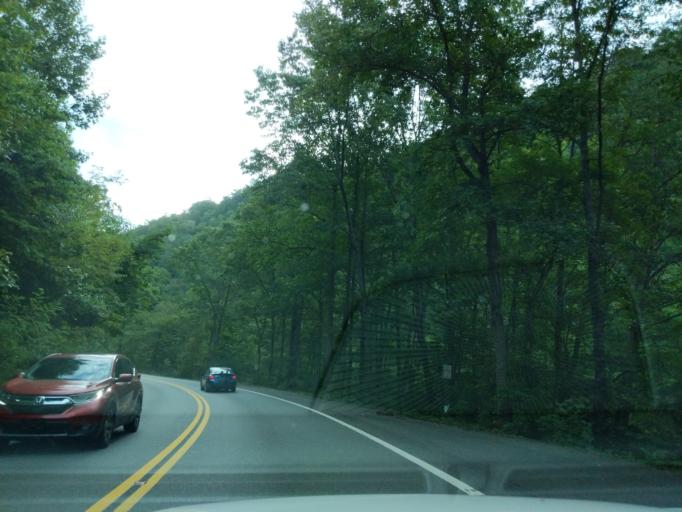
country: US
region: Georgia
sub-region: Fannin County
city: McCaysville
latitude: 35.0738
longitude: -84.5051
